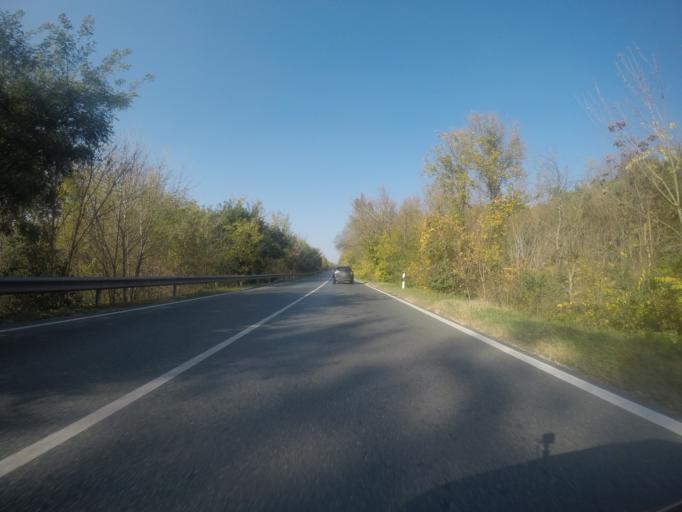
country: HU
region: Tolna
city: Paks
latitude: 46.6891
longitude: 18.8879
